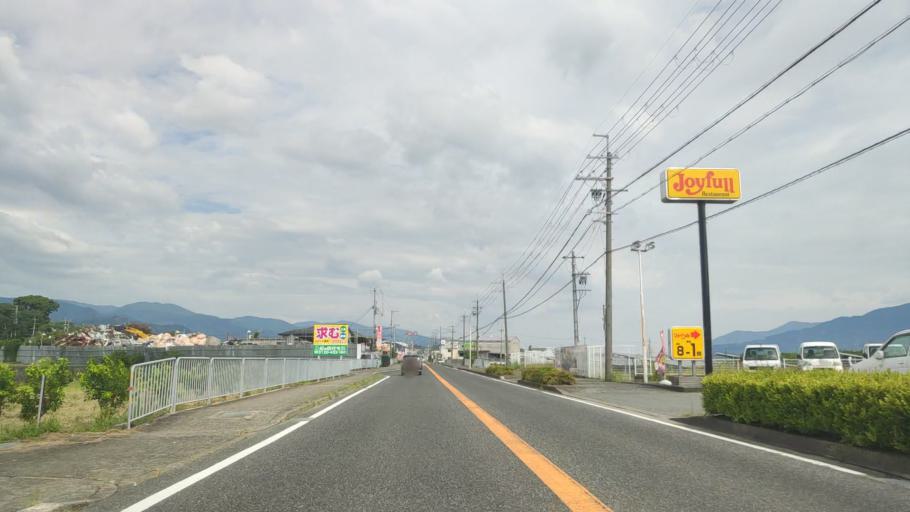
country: JP
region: Wakayama
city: Iwade
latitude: 34.2625
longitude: 135.3841
